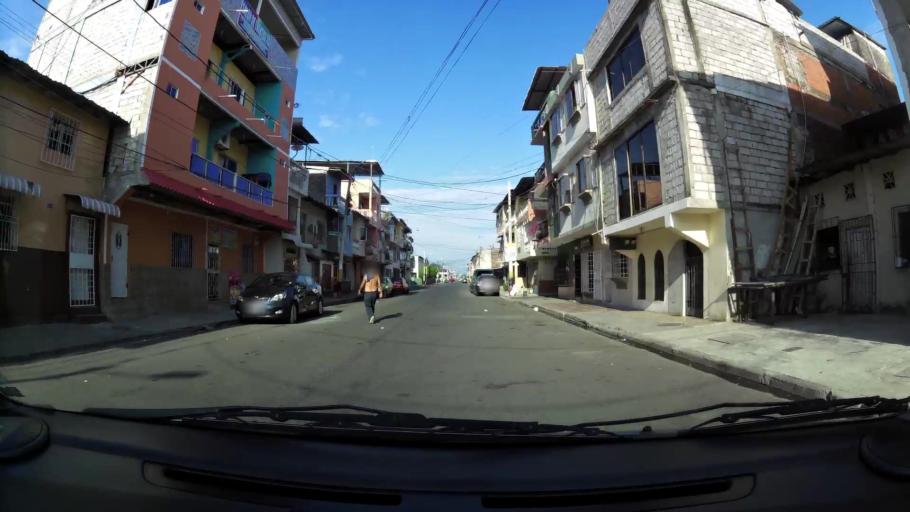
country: EC
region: Guayas
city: Guayaquil
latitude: -2.2091
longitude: -79.9068
